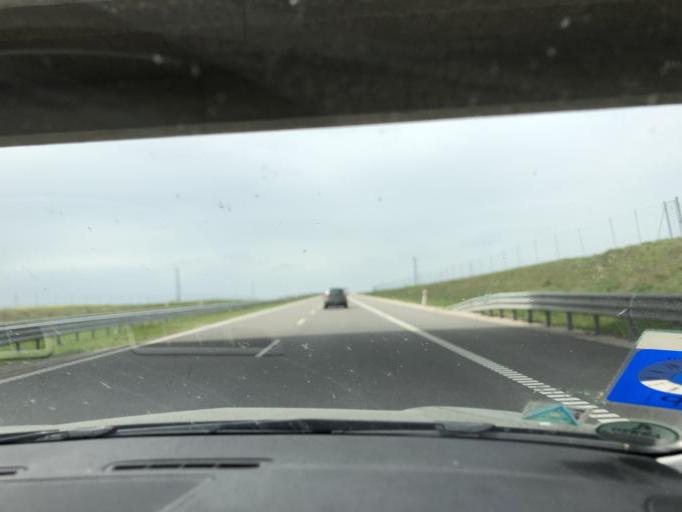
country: PL
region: Subcarpathian Voivodeship
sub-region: Powiat jaroslawski
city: Sosnica
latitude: 49.9159
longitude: 22.8604
